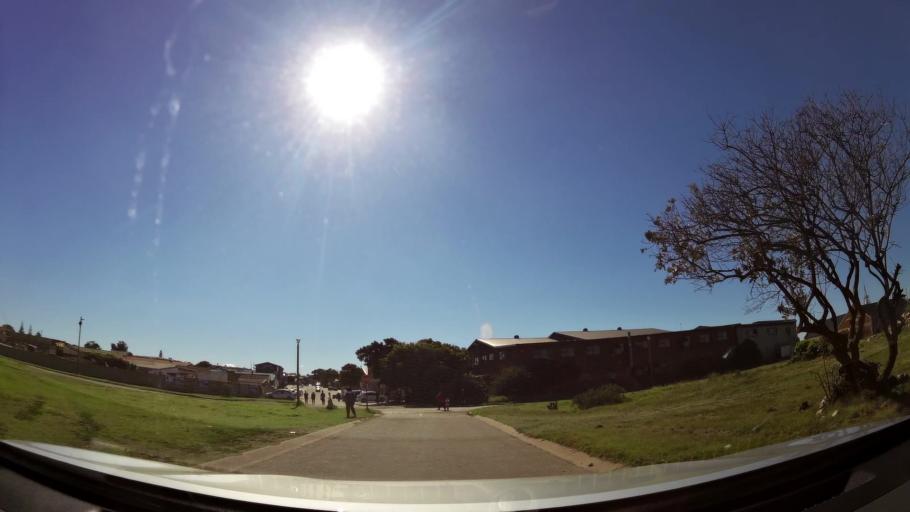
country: ZA
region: Eastern Cape
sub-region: Cacadu District Municipality
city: Jeffrey's Bay
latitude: -34.0578
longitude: 24.9214
